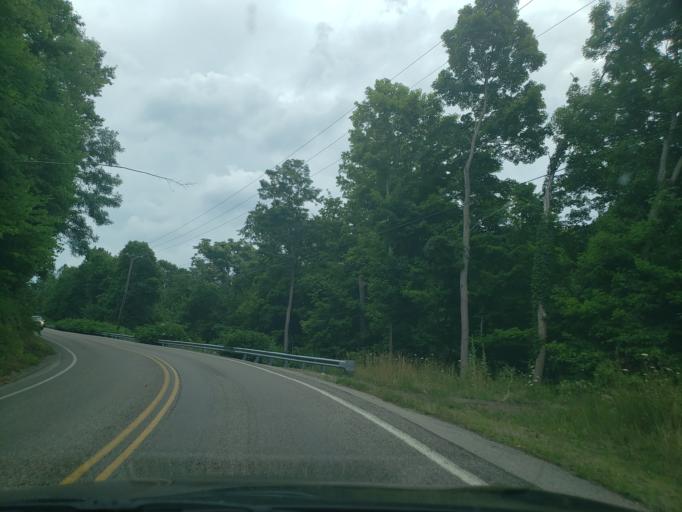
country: US
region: Pennsylvania
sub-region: Allegheny County
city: Avalon
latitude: 40.5066
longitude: -80.0633
